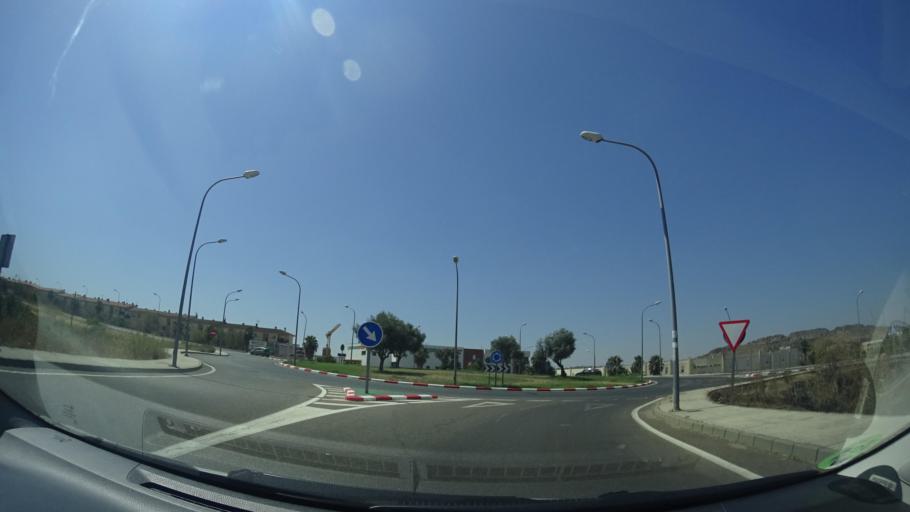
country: ES
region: Extremadura
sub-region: Provincia de Badajoz
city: Zafra
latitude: 38.4319
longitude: -6.4204
